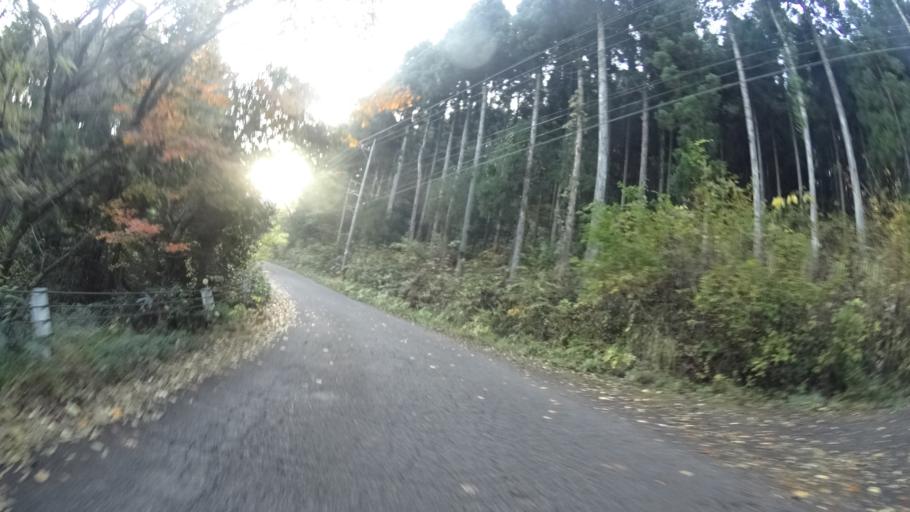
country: JP
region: Ishikawa
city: Nanao
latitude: 37.0206
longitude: 136.9836
